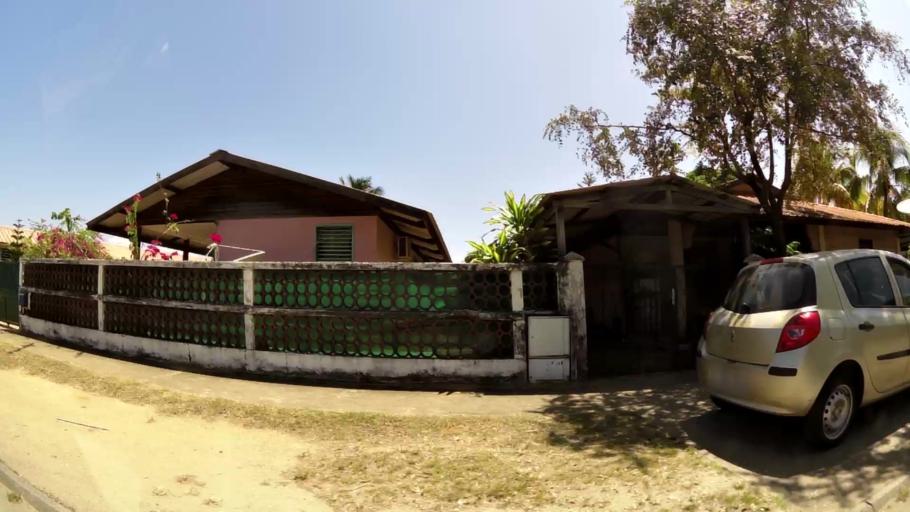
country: GF
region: Guyane
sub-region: Guyane
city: Kourou
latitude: 5.1715
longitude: -52.6554
